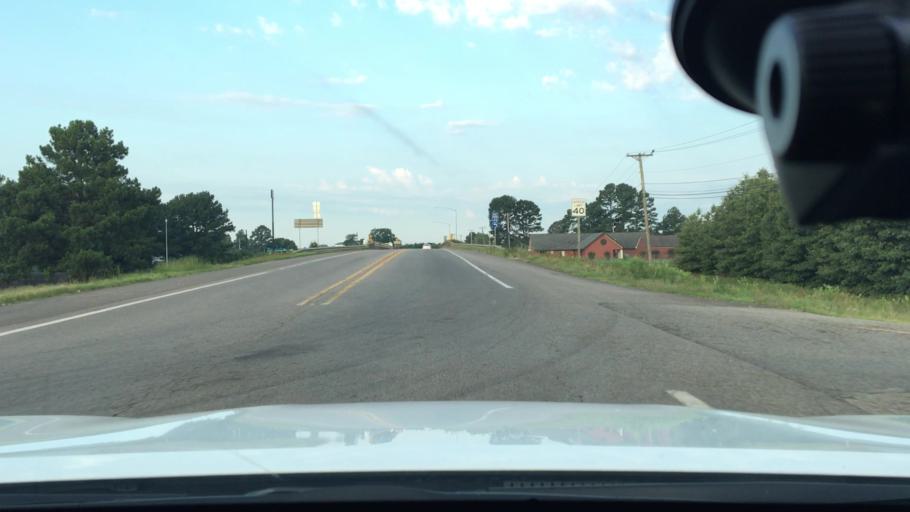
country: US
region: Arkansas
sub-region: Johnson County
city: Clarksville
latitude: 35.4666
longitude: -93.5205
